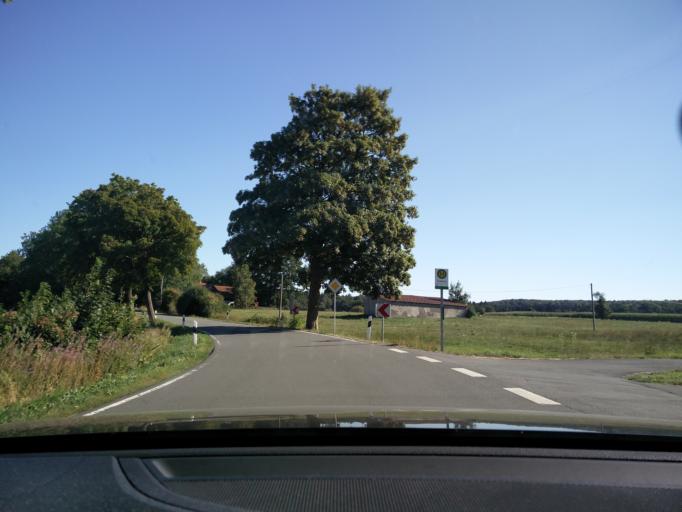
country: DE
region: North Rhine-Westphalia
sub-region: Regierungsbezirk Detmold
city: Altenbeken
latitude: 51.7042
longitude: 8.9419
